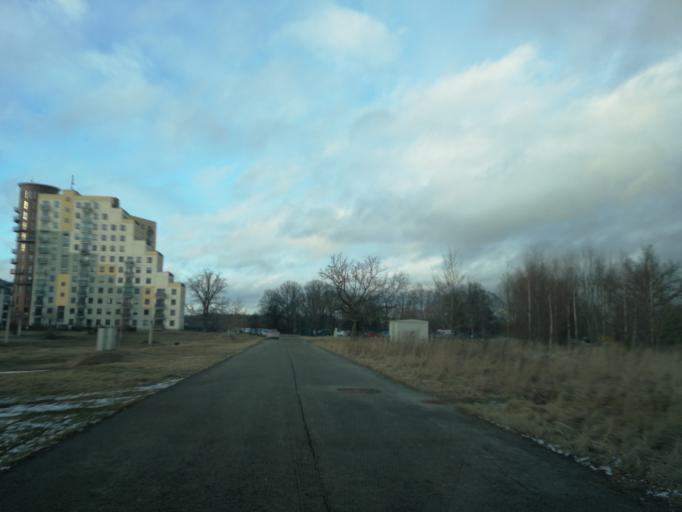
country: LV
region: Adazi
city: Adazi
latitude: 57.0699
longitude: 24.3587
